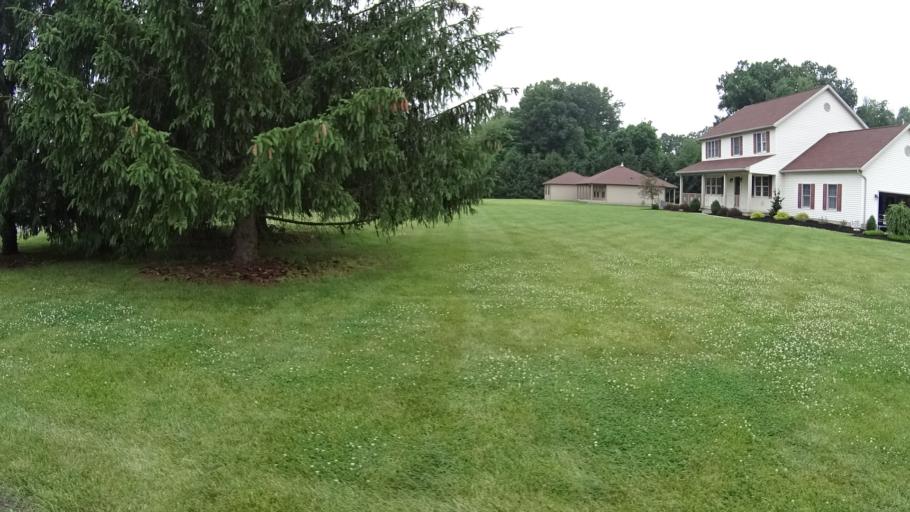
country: US
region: Ohio
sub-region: Erie County
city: Milan
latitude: 41.2984
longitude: -82.5820
